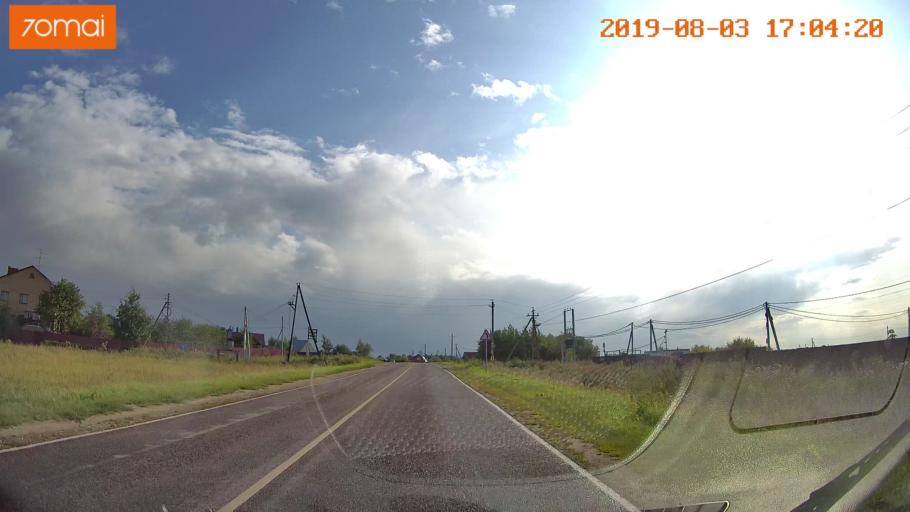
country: RU
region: Moskovskaya
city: Troitskoye
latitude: 55.3295
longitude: 38.5594
